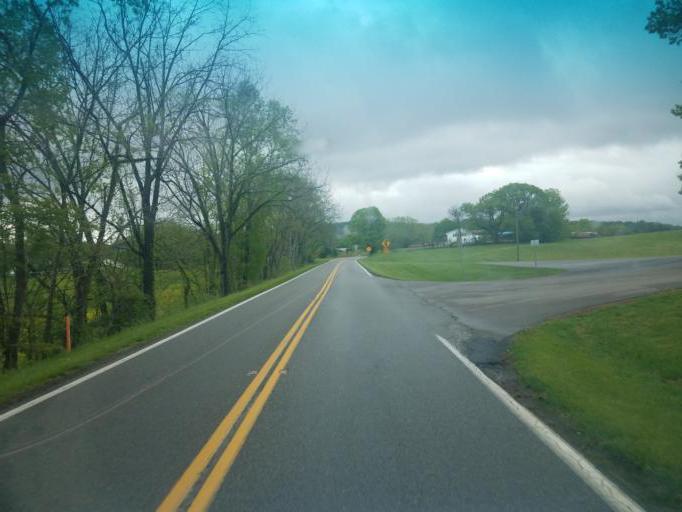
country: US
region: Virginia
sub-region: Washington County
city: Emory
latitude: 36.6549
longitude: -81.7935
